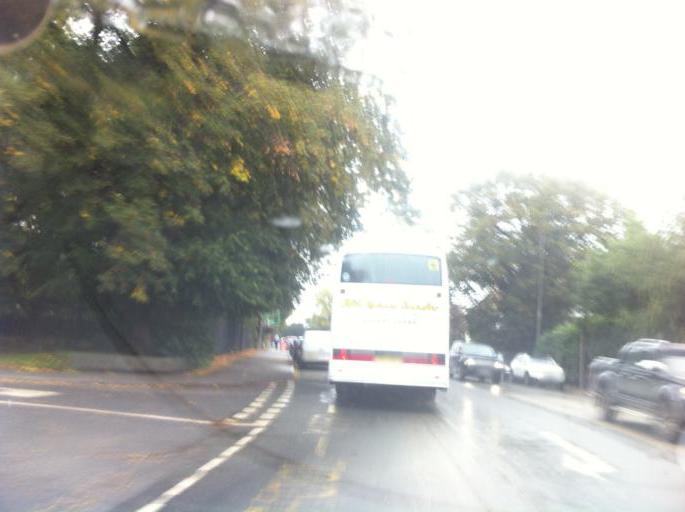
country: GB
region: England
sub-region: Lincolnshire
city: Boston
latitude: 52.9876
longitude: -0.0085
